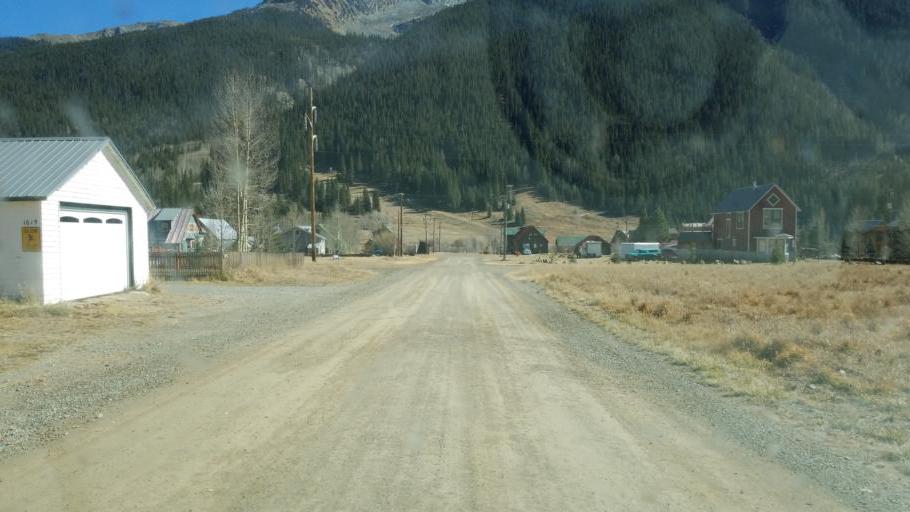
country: US
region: Colorado
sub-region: San Juan County
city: Silverton
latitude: 37.8143
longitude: -107.6602
